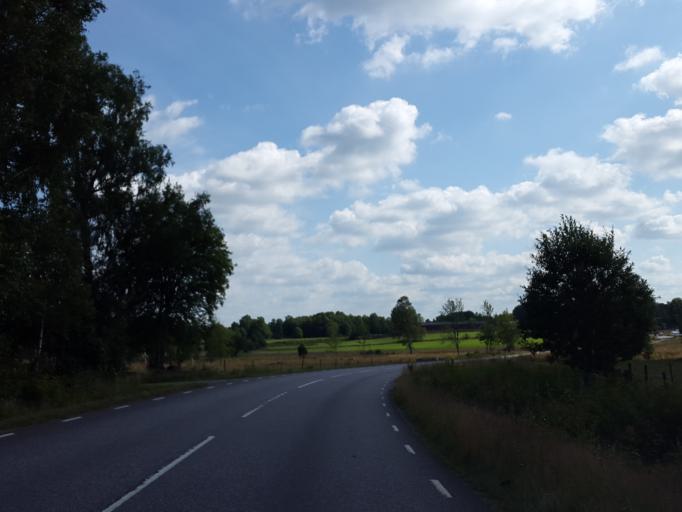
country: SE
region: Vaestra Goetaland
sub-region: Herrljunga Kommun
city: Herrljunga
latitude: 58.0747
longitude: 13.0715
